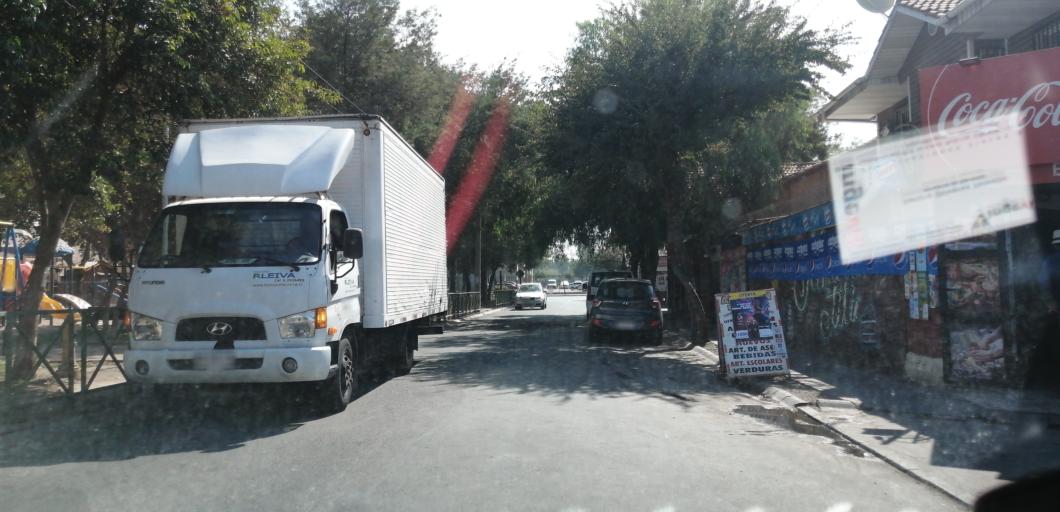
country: CL
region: Santiago Metropolitan
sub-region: Provincia de Santiago
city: Lo Prado
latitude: -33.4538
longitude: -70.7467
